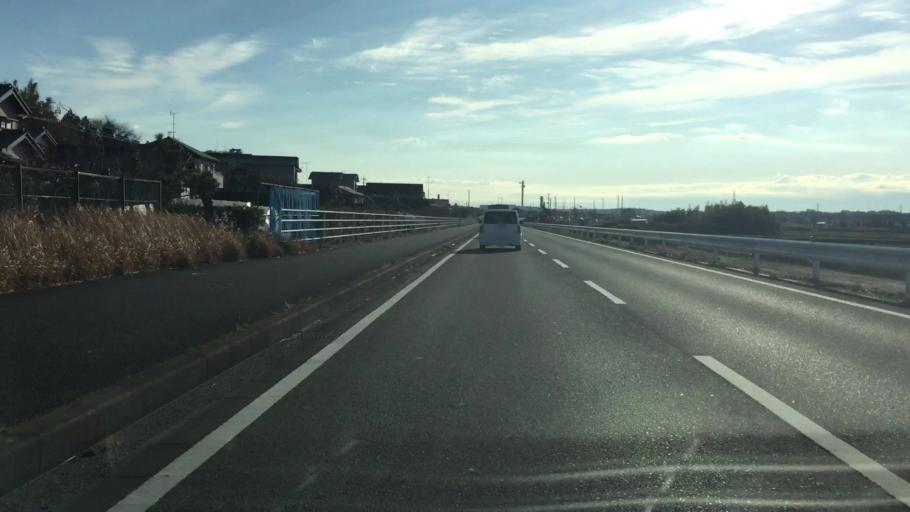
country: JP
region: Ibaraki
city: Toride
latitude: 35.8506
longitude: 140.1267
